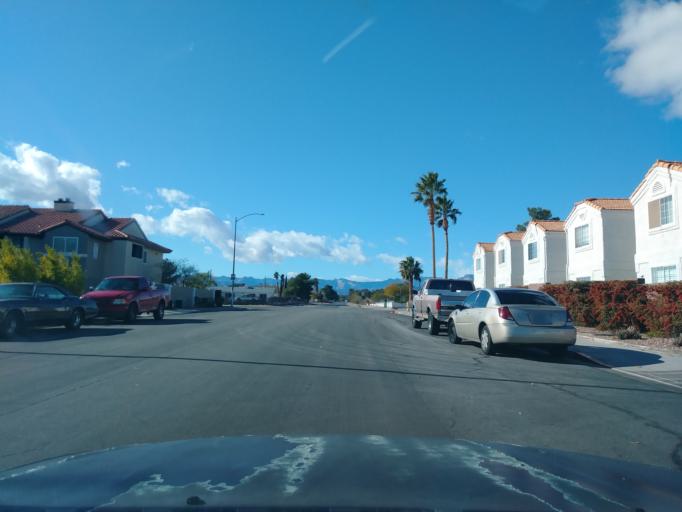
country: US
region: Nevada
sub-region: Clark County
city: Spring Valley
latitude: 36.1500
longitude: -115.2117
